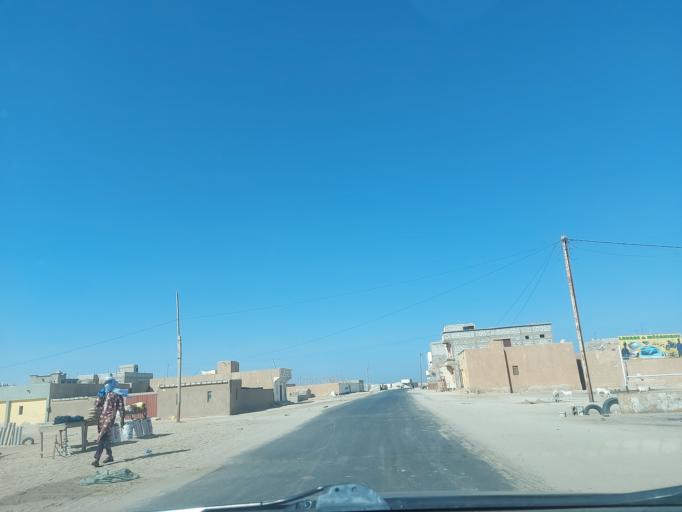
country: MR
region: Nouakchott
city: Nouakchott
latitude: 18.0615
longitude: -16.0052
